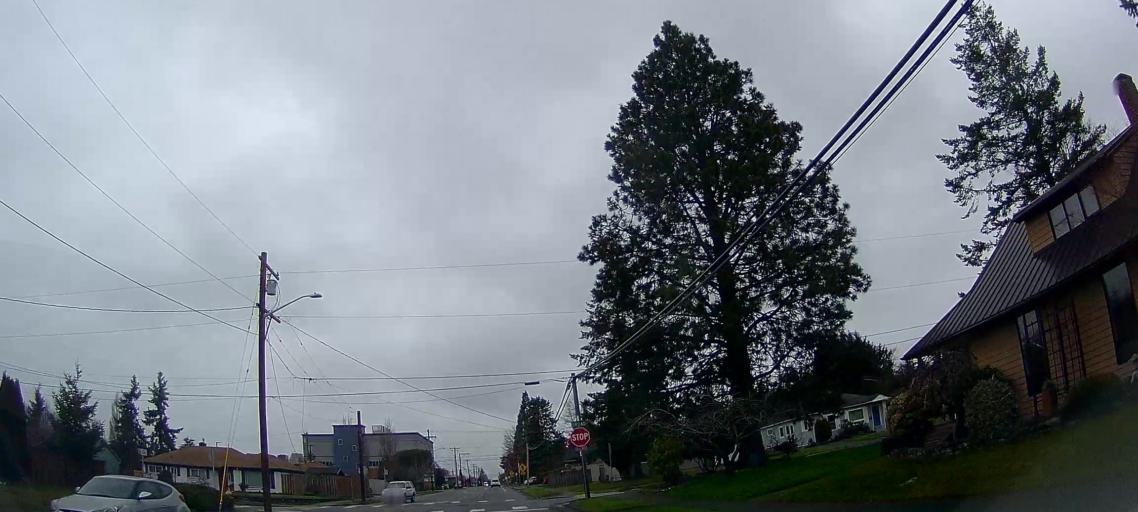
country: US
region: Washington
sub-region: Skagit County
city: Mount Vernon
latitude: 48.4153
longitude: -122.3229
